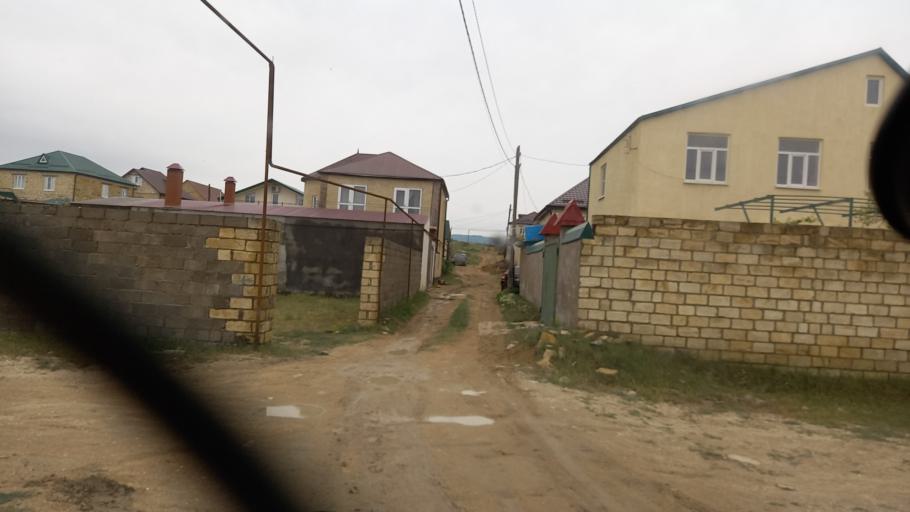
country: RU
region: Dagestan
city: Sabnova
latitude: 42.1187
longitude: 48.2654
